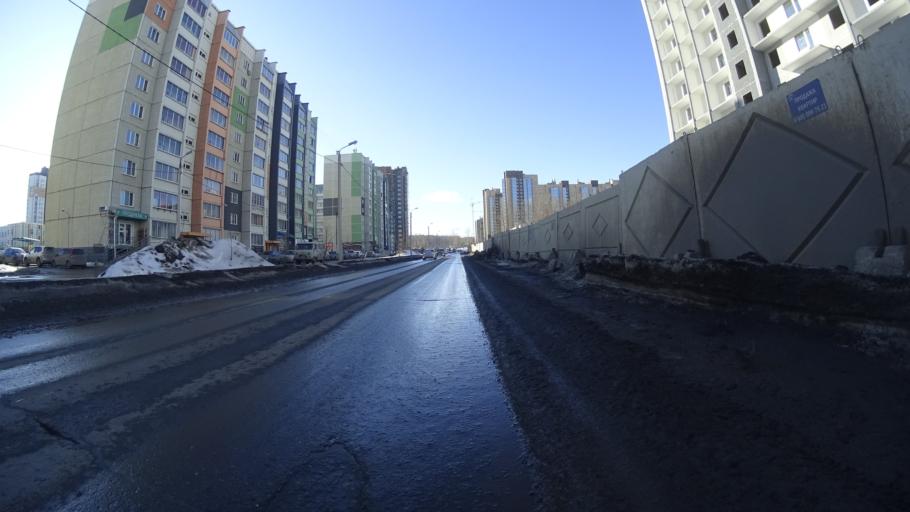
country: RU
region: Chelyabinsk
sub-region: Gorod Chelyabinsk
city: Chelyabinsk
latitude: 55.1671
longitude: 61.2888
